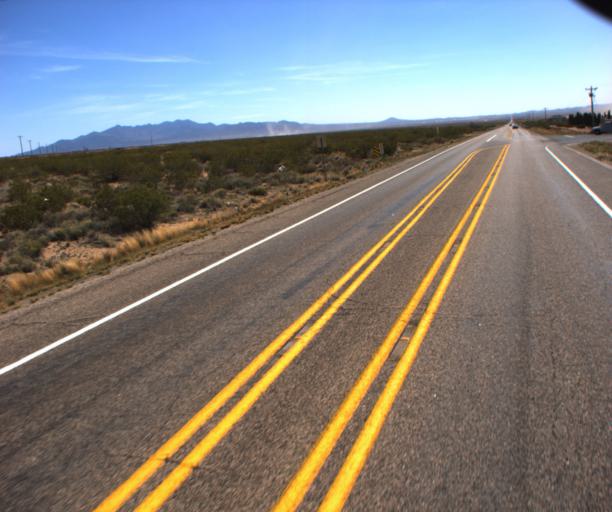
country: US
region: Arizona
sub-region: Mohave County
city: New Kingman-Butler
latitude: 35.3822
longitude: -113.8528
